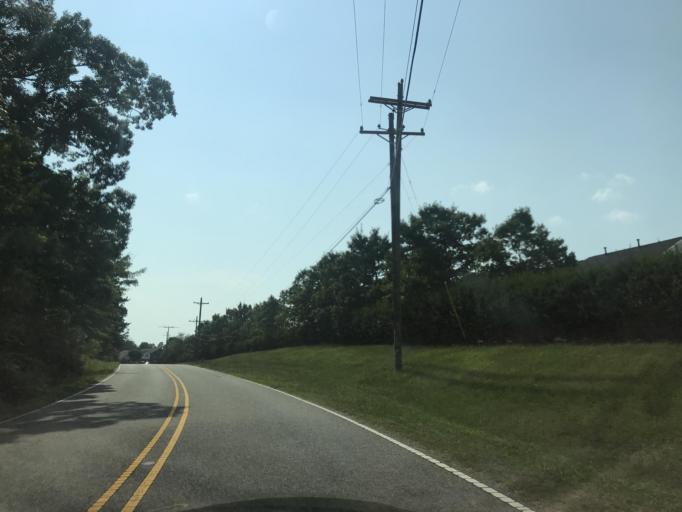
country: US
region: North Carolina
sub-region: Wake County
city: Morrisville
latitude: 35.8384
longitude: -78.8666
